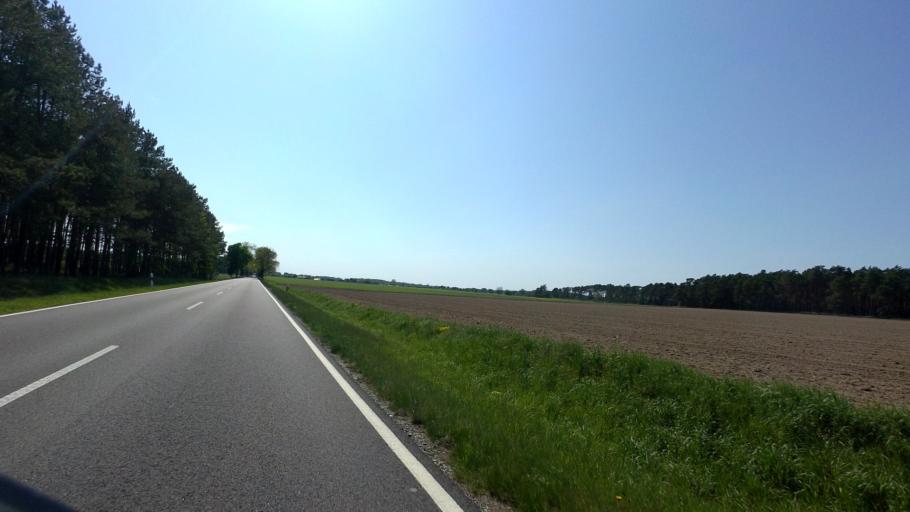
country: DE
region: Brandenburg
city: Neu Zauche
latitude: 52.0363
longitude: 14.1021
